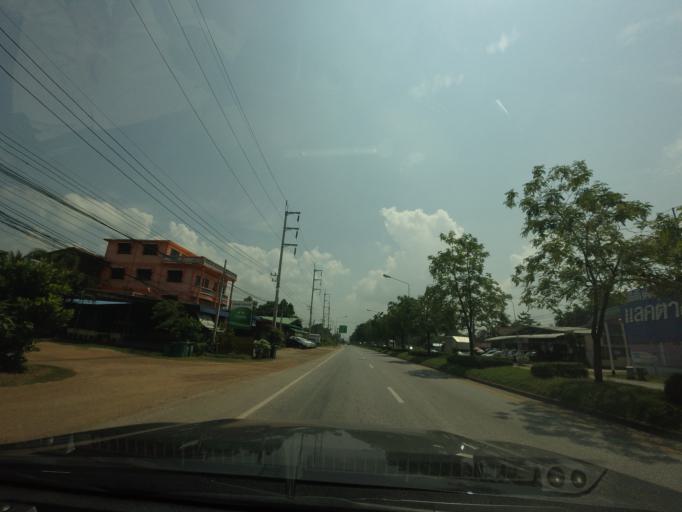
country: TH
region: Uttaradit
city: Uttaradit
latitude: 17.5892
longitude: 100.1350
